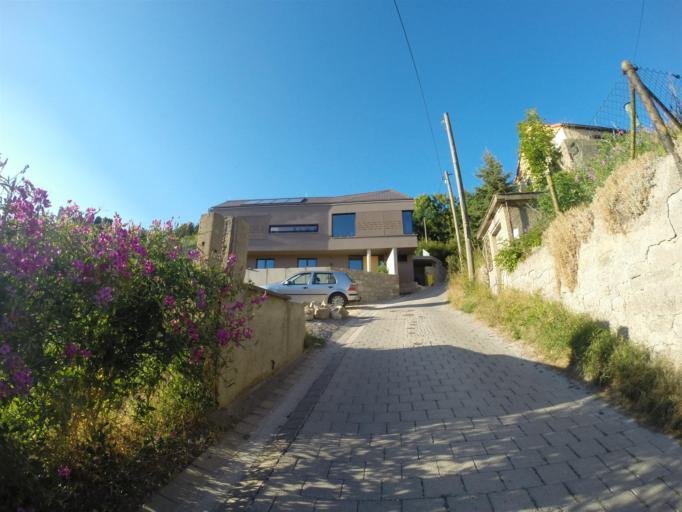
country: DE
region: Thuringia
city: Jena
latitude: 50.9209
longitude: 11.6248
